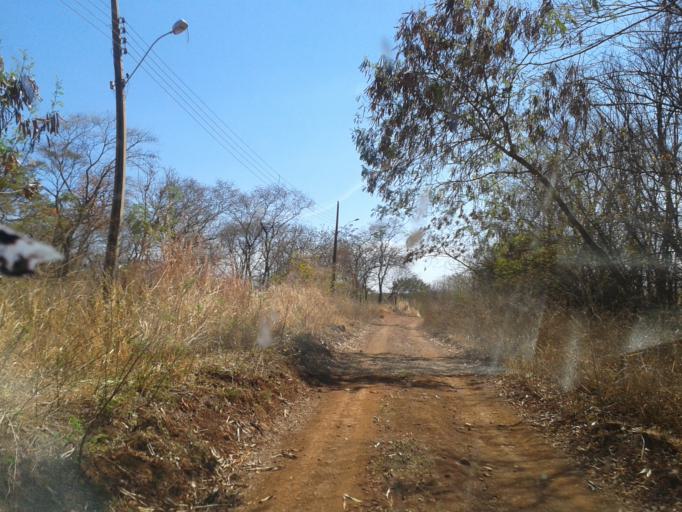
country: BR
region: Minas Gerais
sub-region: Capinopolis
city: Capinopolis
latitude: -18.6877
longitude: -49.5842
